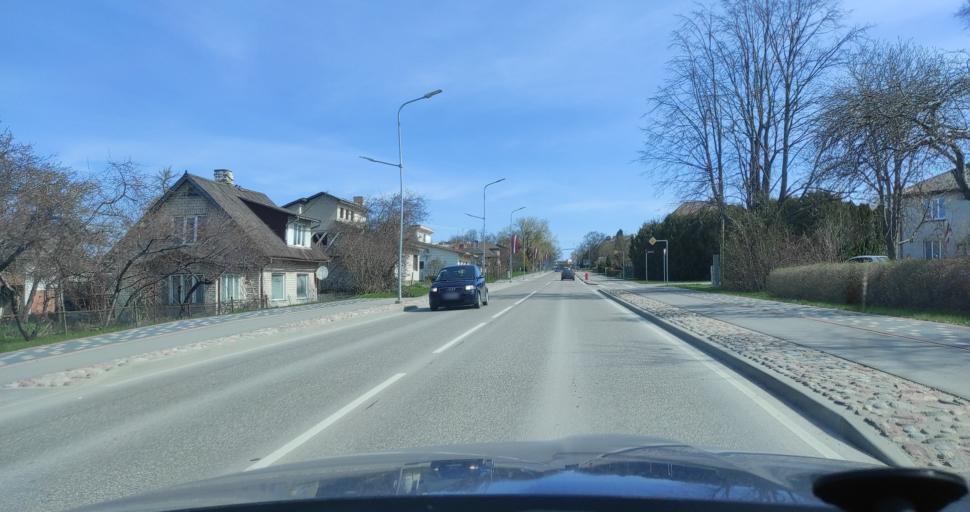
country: LV
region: Talsu Rajons
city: Talsi
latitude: 57.2398
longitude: 22.5763
